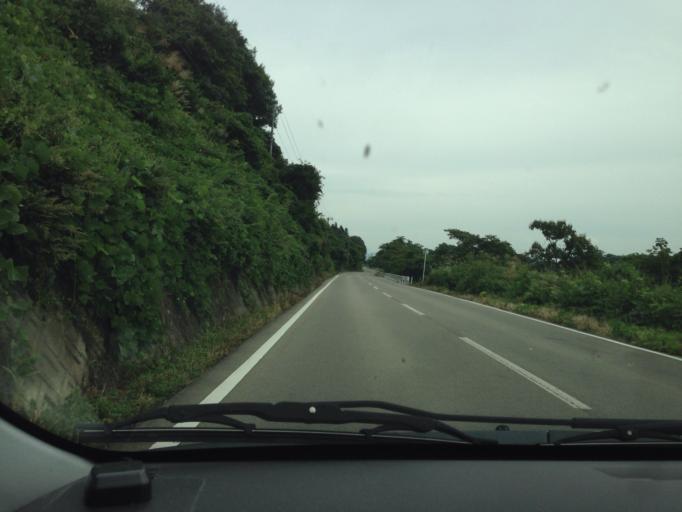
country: JP
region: Fukushima
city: Kitakata
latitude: 37.6132
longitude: 139.8085
